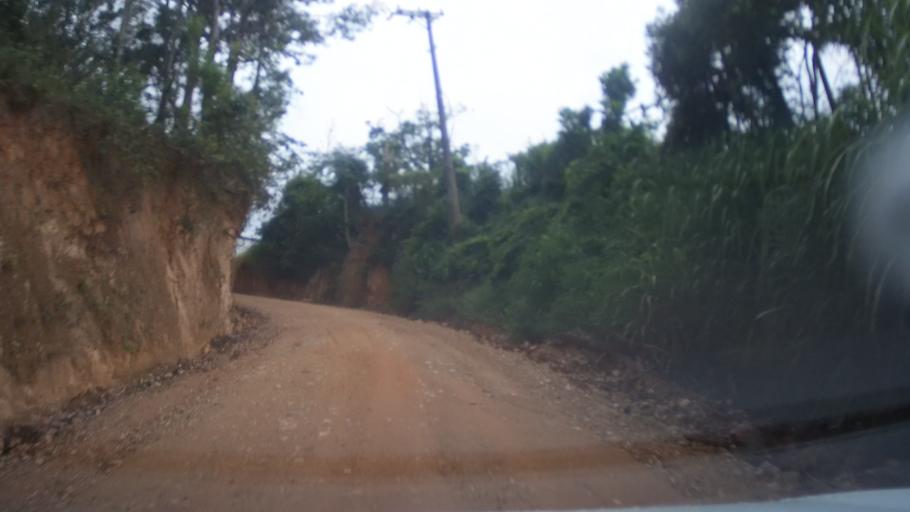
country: BR
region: Sao Paulo
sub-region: Itupeva
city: Itupeva
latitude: -23.1788
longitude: -47.0764
